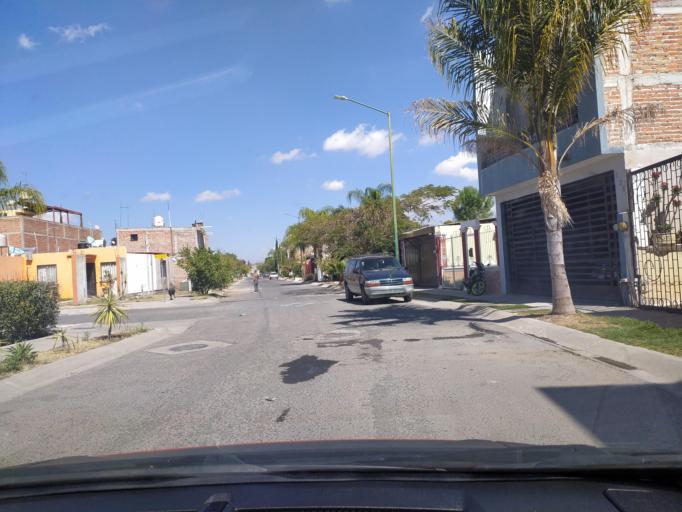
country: LA
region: Oudomxai
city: Muang La
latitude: 21.0276
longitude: 101.8279
